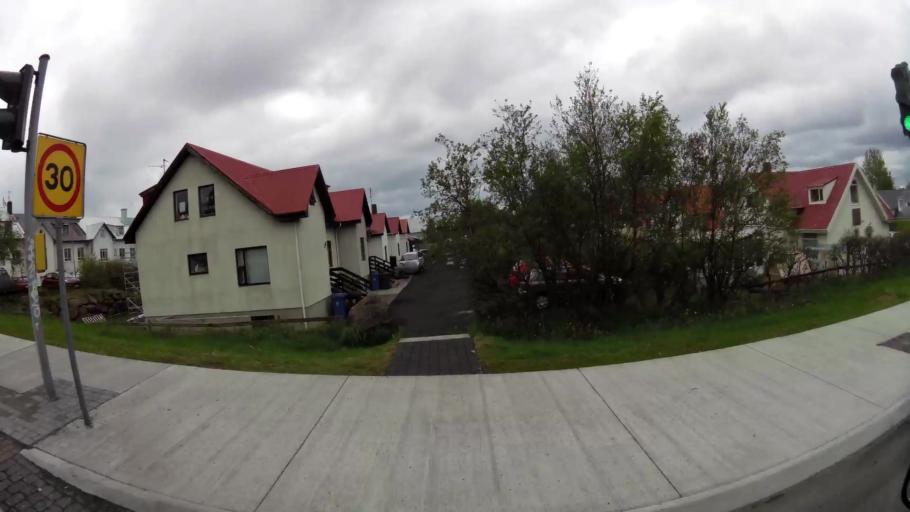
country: IS
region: Capital Region
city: Reykjavik
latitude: 64.1250
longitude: -21.8650
